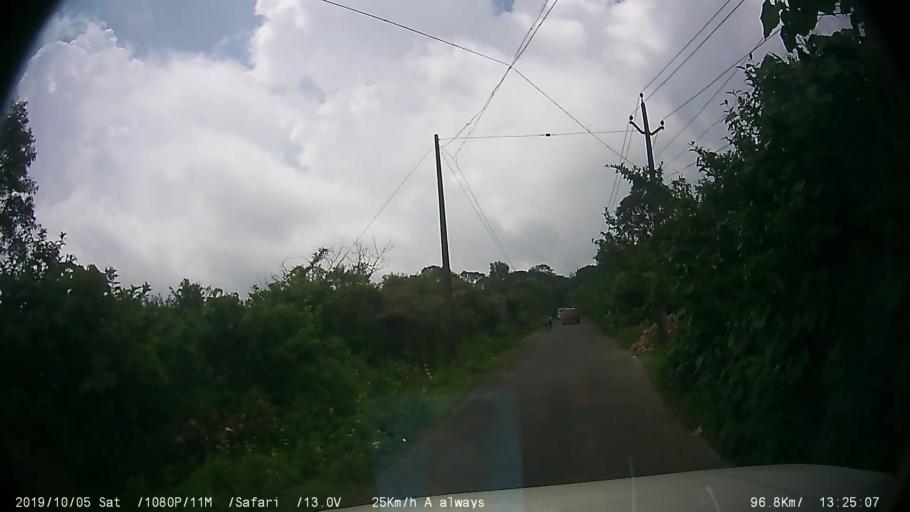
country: IN
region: Kerala
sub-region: Kottayam
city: Erattupetta
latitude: 9.5769
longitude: 76.9708
